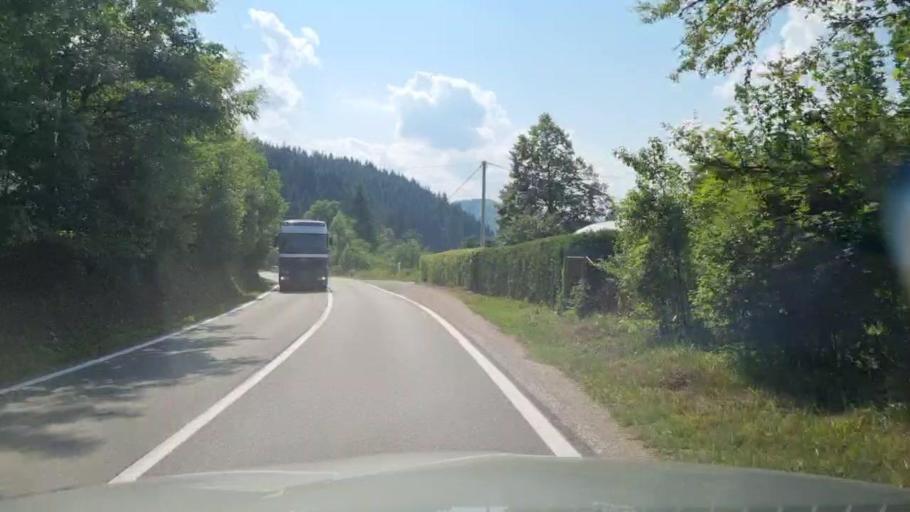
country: BA
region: Federation of Bosnia and Herzegovina
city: Olovo
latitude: 44.1278
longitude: 18.5955
